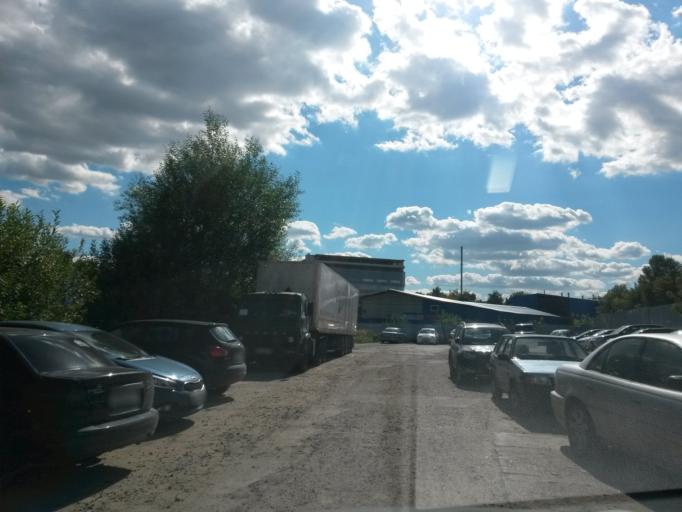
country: RU
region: Moskovskaya
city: Kozhukhovo
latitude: 55.7022
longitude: 37.6991
